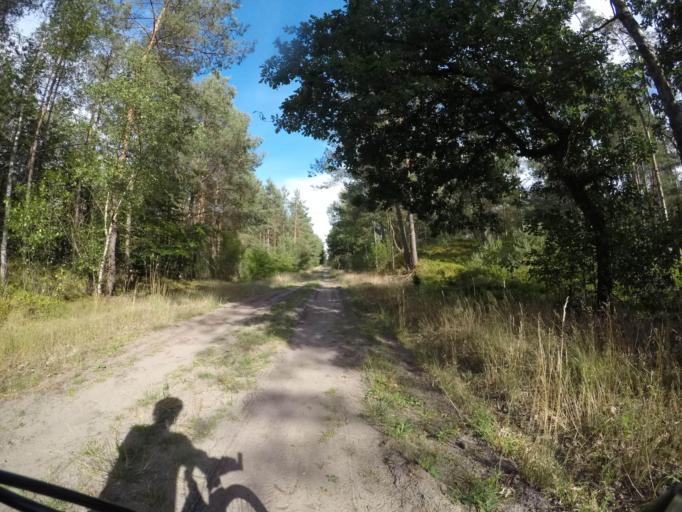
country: DE
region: Lower Saxony
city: Neu Darchau
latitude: 53.2746
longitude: 10.9625
